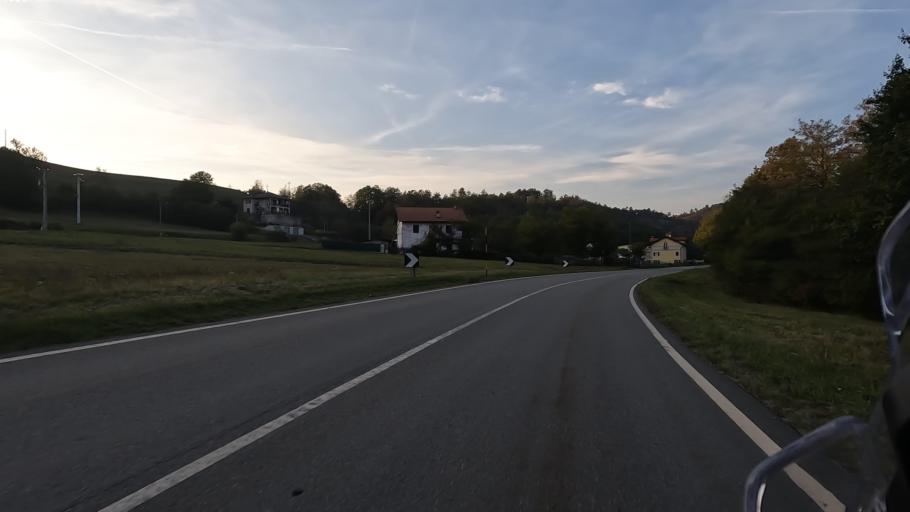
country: IT
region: Liguria
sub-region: Provincia di Savona
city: Sassello
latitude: 44.5111
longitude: 8.4744
